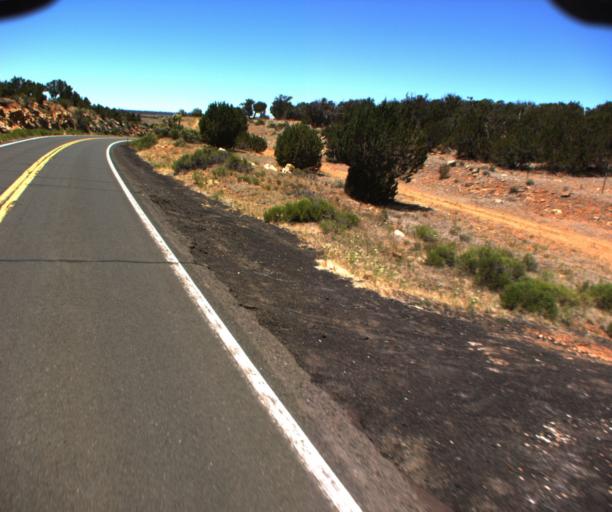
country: US
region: Arizona
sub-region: Coconino County
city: LeChee
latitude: 34.7303
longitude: -111.0728
